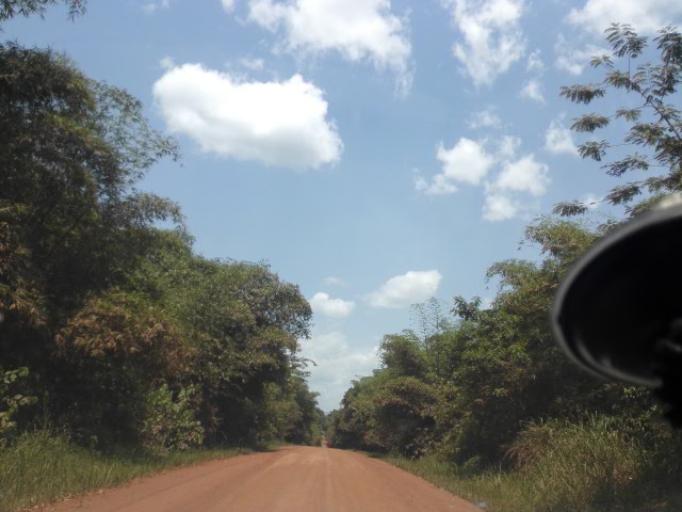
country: CD
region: Eastern Province
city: Kisangani
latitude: 0.6285
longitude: 26.0690
